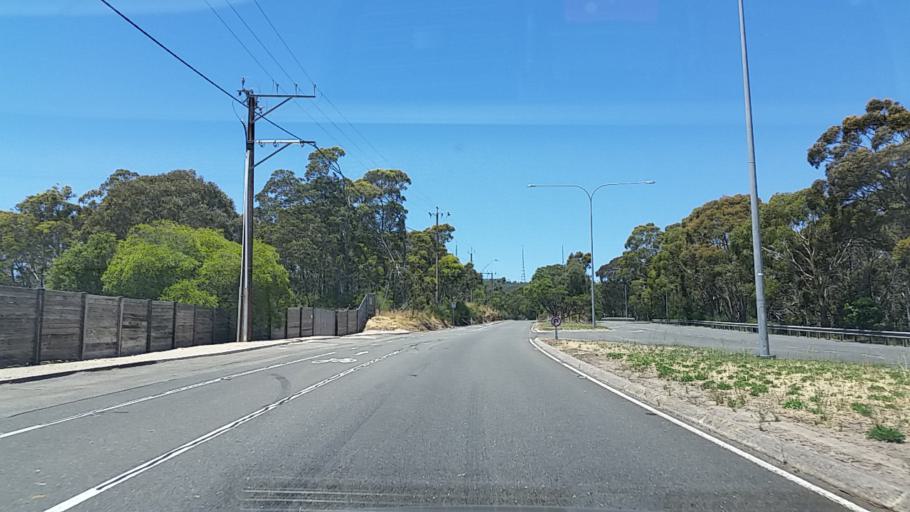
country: AU
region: South Australia
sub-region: Burnside
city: Mount Osmond
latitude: -34.9755
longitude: 138.6796
